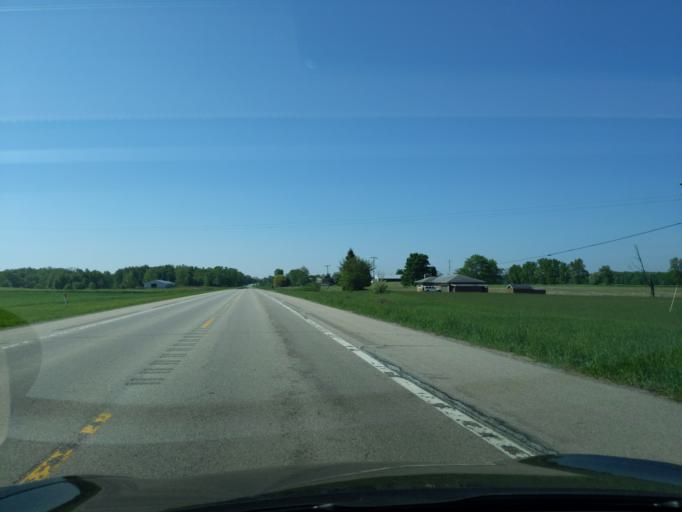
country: US
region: Michigan
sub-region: Ingham County
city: Stockbridge
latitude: 42.5238
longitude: -84.1906
